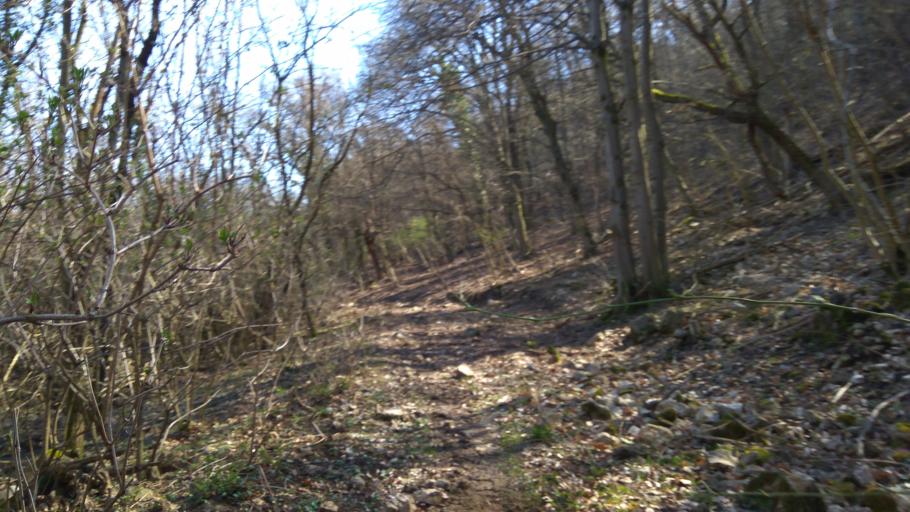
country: HU
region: Pest
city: Csobanka
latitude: 47.6345
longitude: 18.9833
